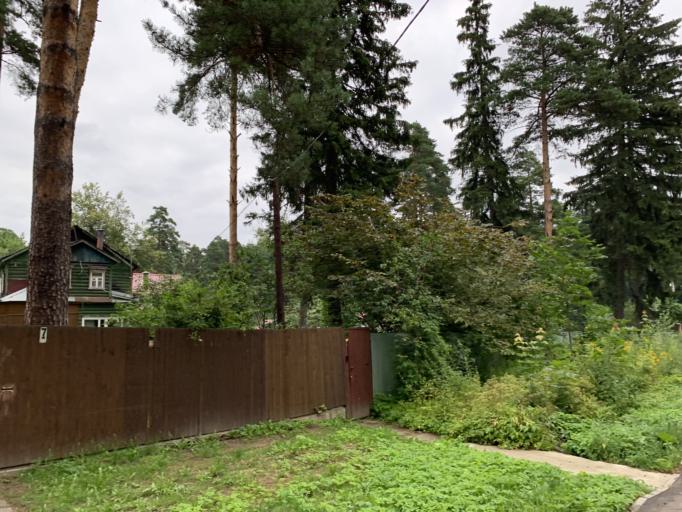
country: RU
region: Moskovskaya
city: Mamontovka
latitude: 55.9757
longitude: 37.8293
